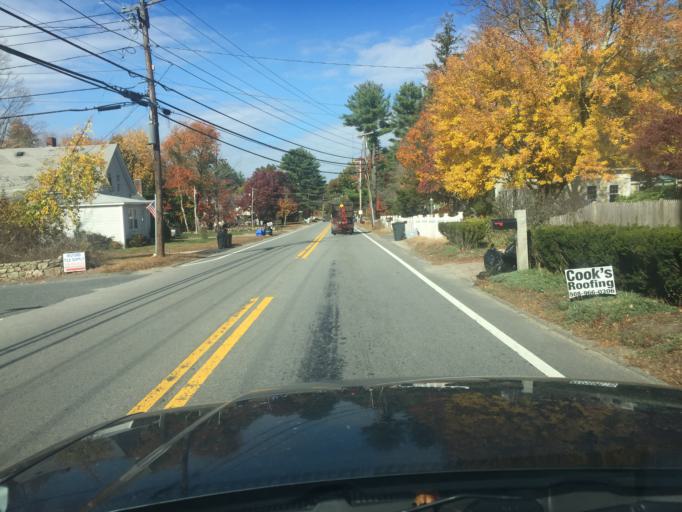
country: US
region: Massachusetts
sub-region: Norfolk County
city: Bellingham
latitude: 42.1048
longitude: -71.5047
